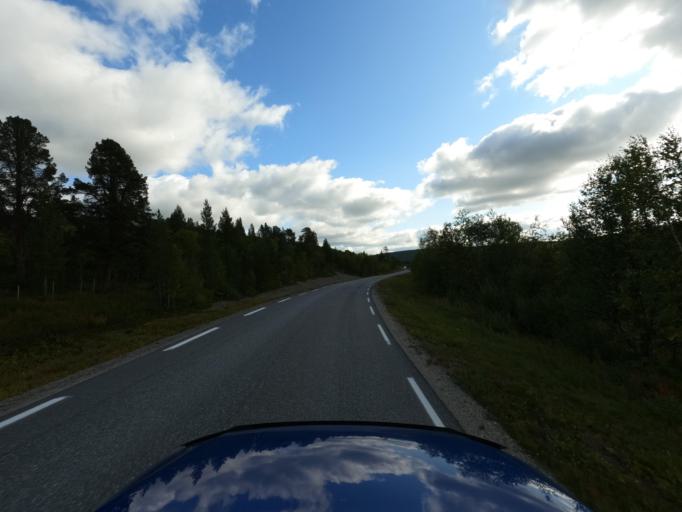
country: NO
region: Finnmark Fylke
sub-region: Karasjok
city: Karasjohka
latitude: 69.4306
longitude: 24.8998
